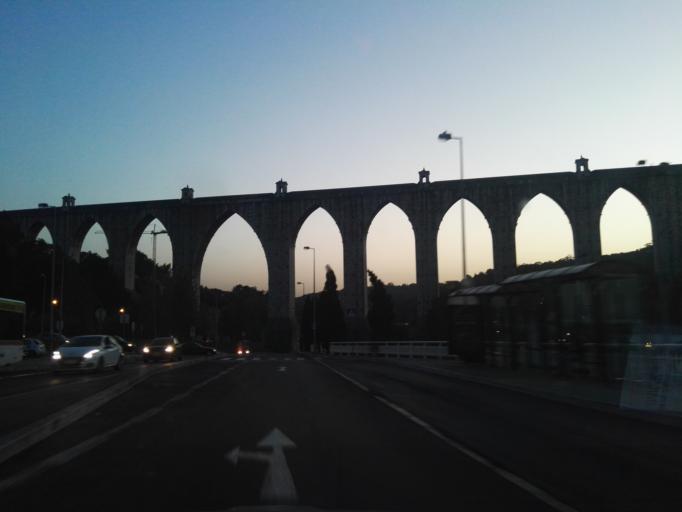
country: PT
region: Lisbon
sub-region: Lisbon
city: Lisbon
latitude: 38.7310
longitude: -9.1684
